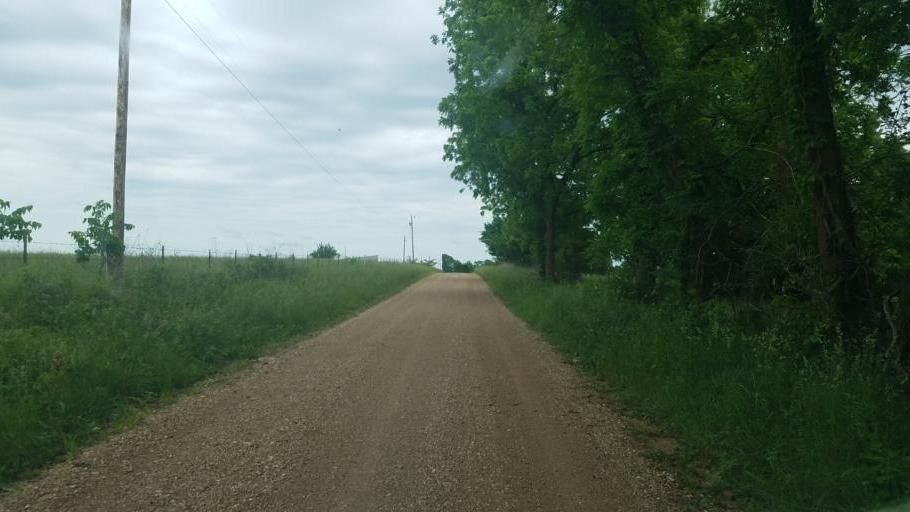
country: US
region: Missouri
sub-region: Moniteau County
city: Tipton
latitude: 38.5949
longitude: -92.6827
